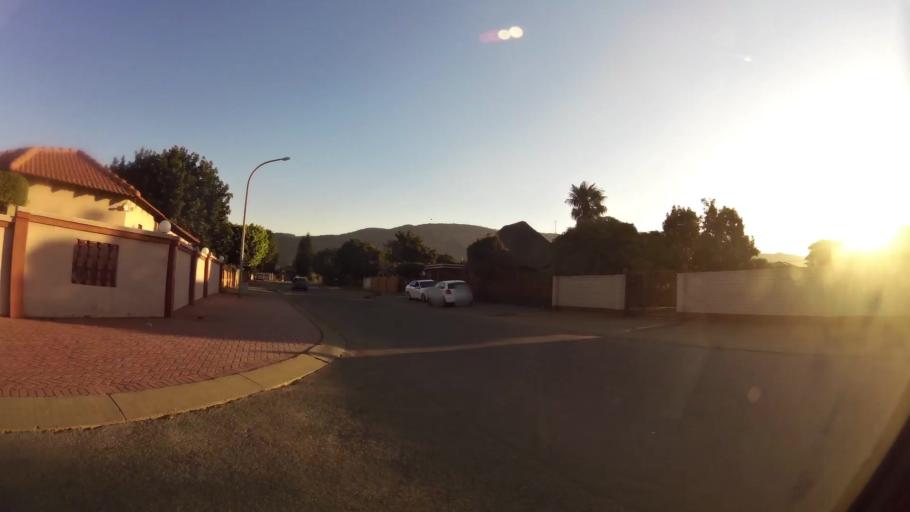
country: ZA
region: North-West
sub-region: Bojanala Platinum District Municipality
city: Rustenburg
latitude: -25.6416
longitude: 27.2084
